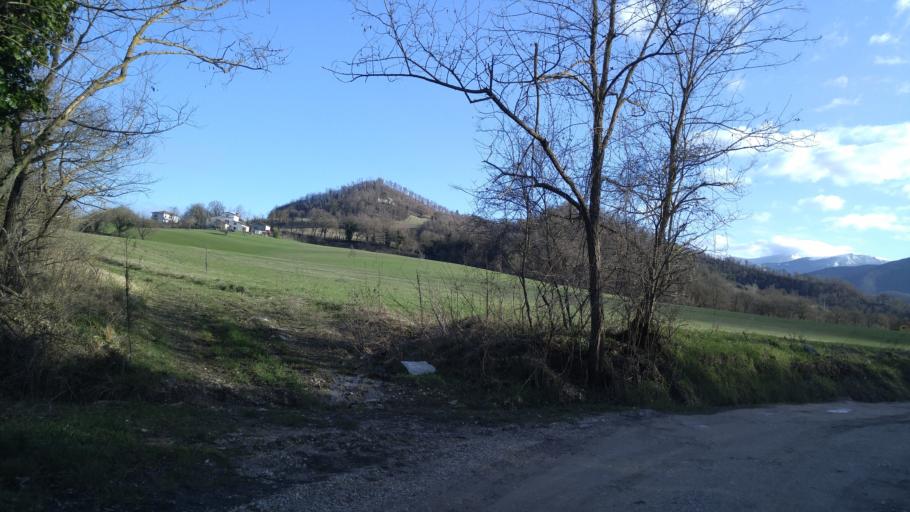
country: IT
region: The Marches
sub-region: Provincia di Pesaro e Urbino
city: Cagli
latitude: 43.5588
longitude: 12.6577
